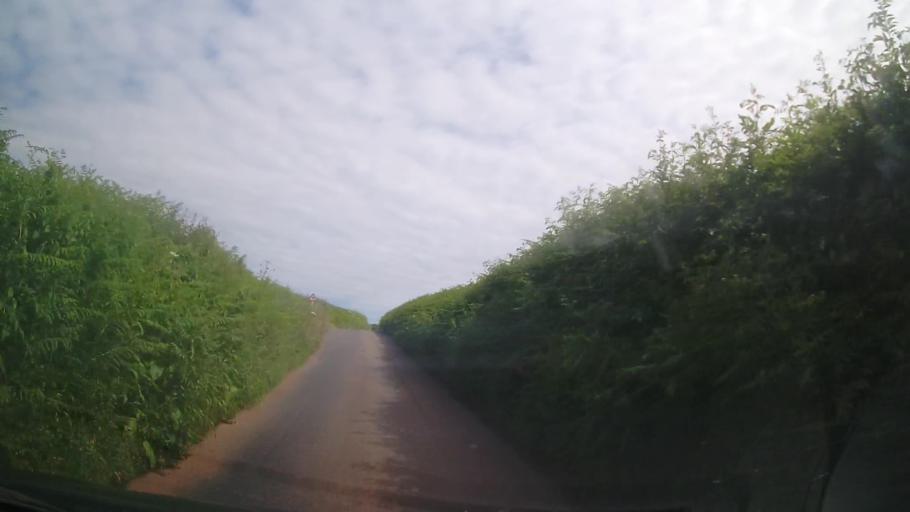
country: GB
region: England
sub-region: Devon
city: Salcombe
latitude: 50.2384
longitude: -3.6771
